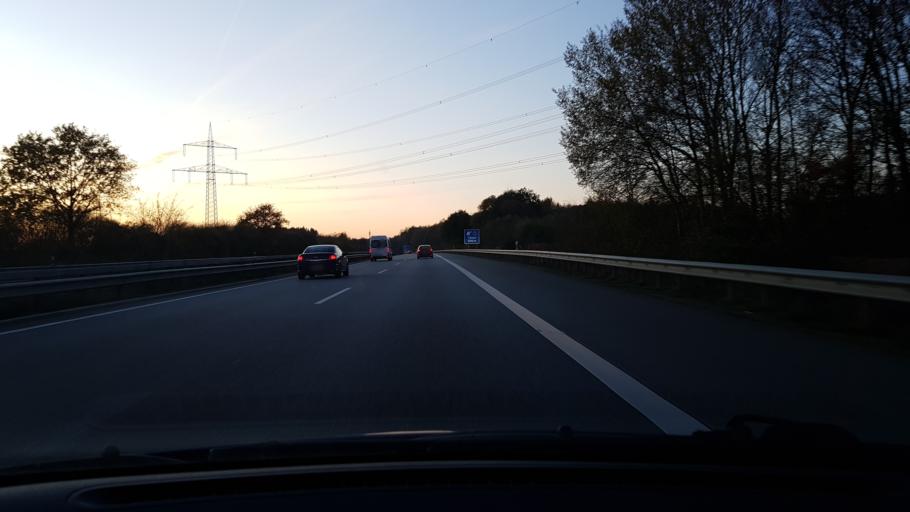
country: DE
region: Schleswig-Holstein
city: Talkau
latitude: 53.5590
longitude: 10.5776
